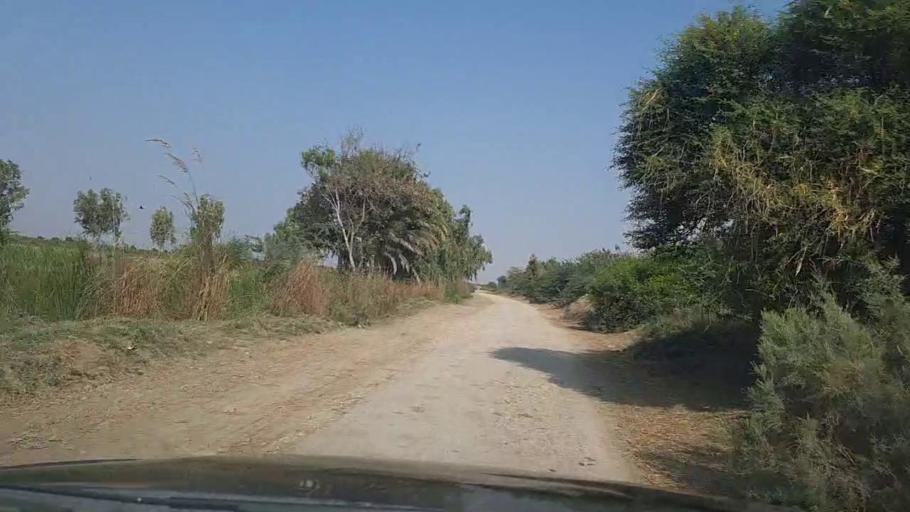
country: PK
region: Sindh
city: Thatta
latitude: 24.6330
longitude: 67.8135
